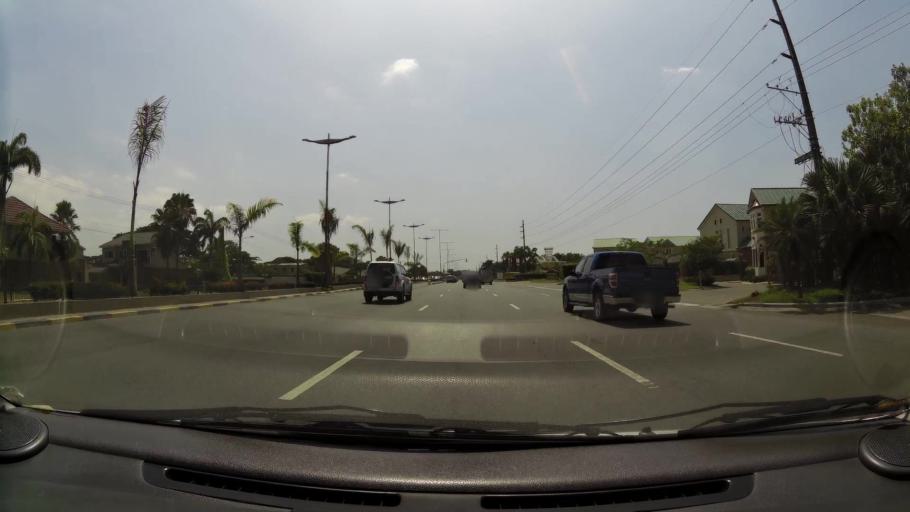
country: EC
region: Guayas
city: Eloy Alfaro
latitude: -2.1079
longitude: -79.8721
